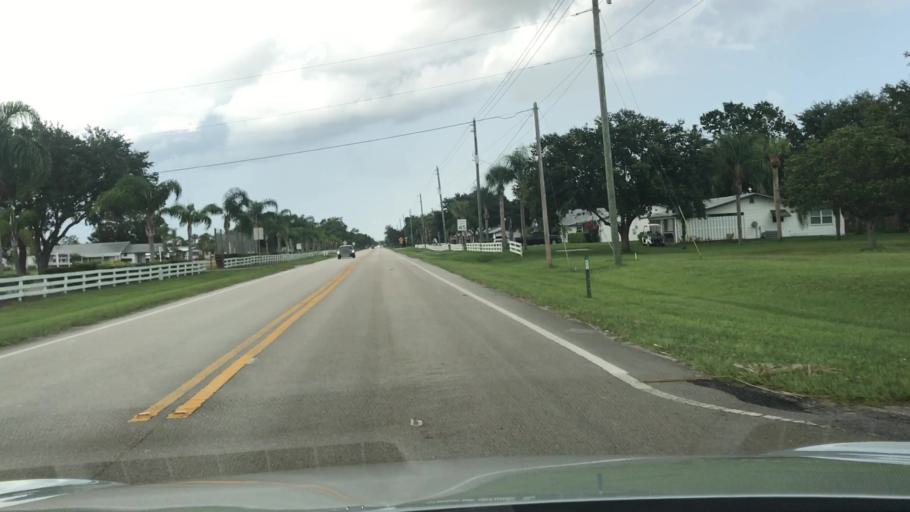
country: US
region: Florida
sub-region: Indian River County
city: Sebastian
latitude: 27.7901
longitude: -80.4992
